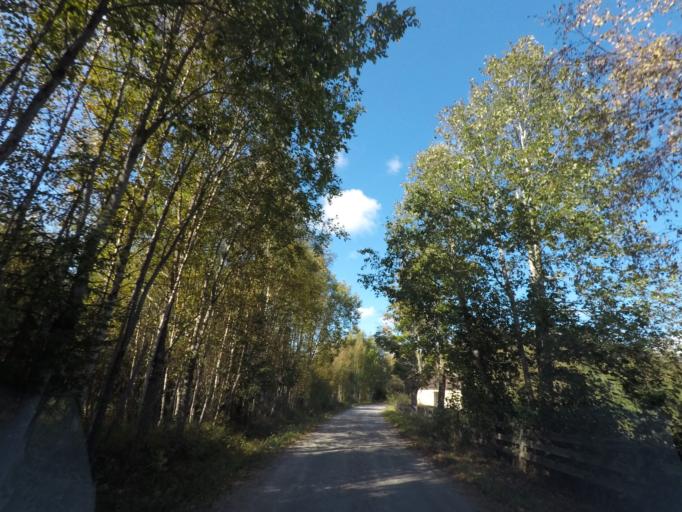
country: SE
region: Vaestmanland
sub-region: Skinnskattebergs Kommun
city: Skinnskatteberg
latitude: 59.8307
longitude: 15.5280
